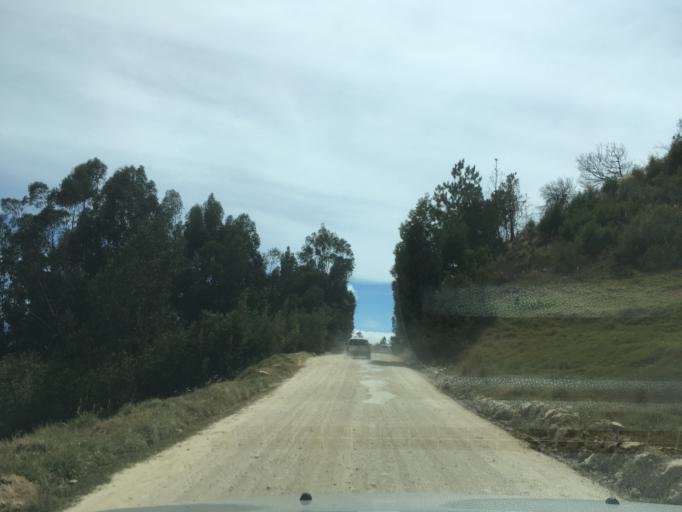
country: CO
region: Boyaca
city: Aquitania
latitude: 5.5888
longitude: -72.9213
